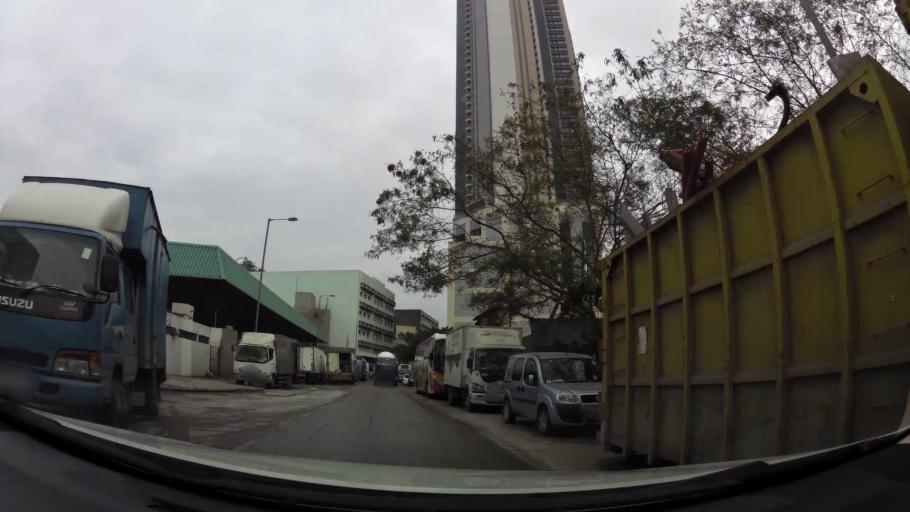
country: HK
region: Kowloon City
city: Kowloon
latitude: 22.2931
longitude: 114.2348
